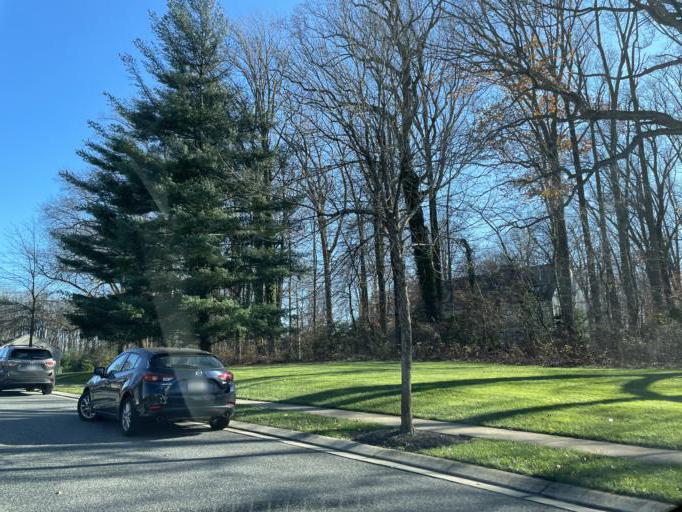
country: US
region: Maryland
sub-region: Baltimore County
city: Pikesville
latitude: 39.3728
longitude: -76.6670
